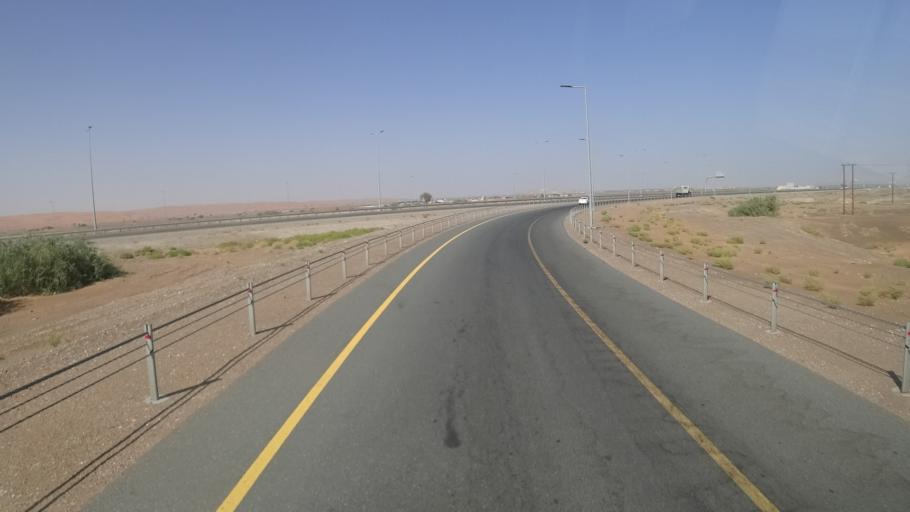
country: OM
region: Ash Sharqiyah
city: Al Qabil
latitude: 22.5253
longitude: 58.7412
